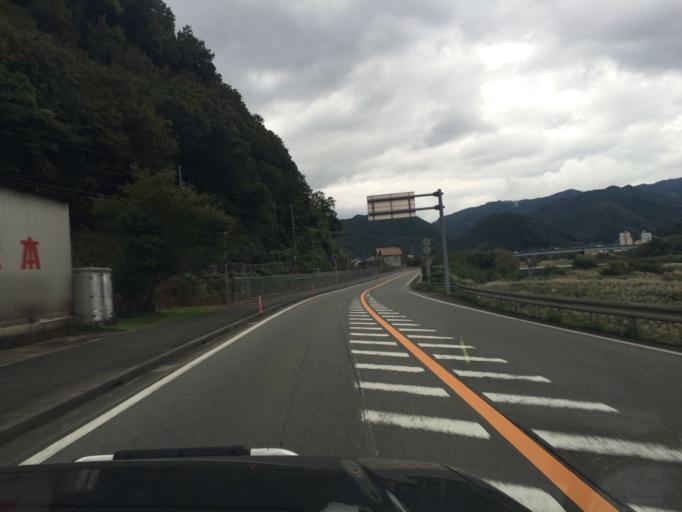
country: JP
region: Hyogo
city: Toyooka
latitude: 35.4175
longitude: 134.7854
